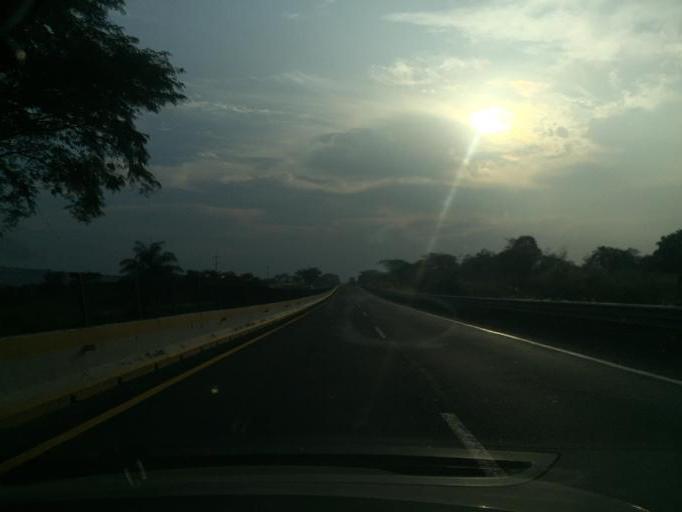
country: MX
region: Veracruz
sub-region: Omealca
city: Mata Tenatito (Casco Hacienda)
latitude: 18.7917
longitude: -96.5702
